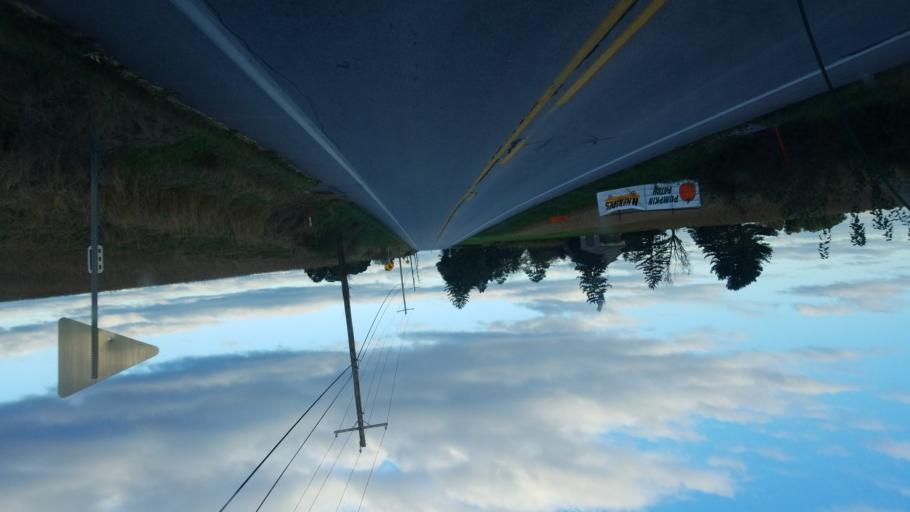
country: US
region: Pennsylvania
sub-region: Adams County
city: East Berlin
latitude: 39.9384
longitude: -77.0058
